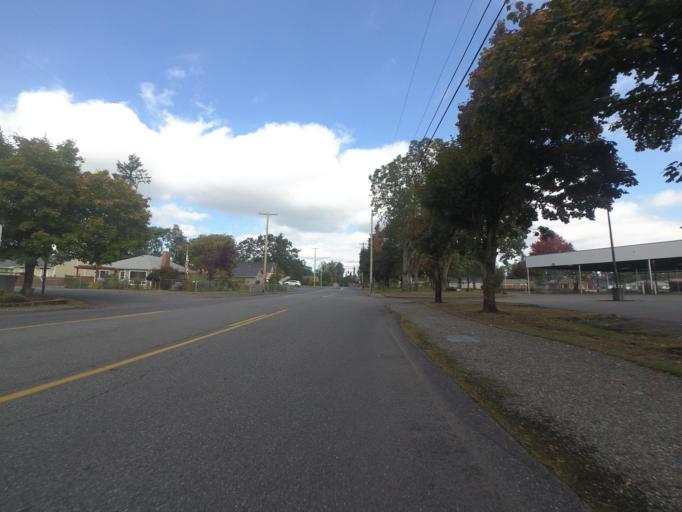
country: US
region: Washington
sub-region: Pierce County
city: Lakewood
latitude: 47.1723
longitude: -122.5218
